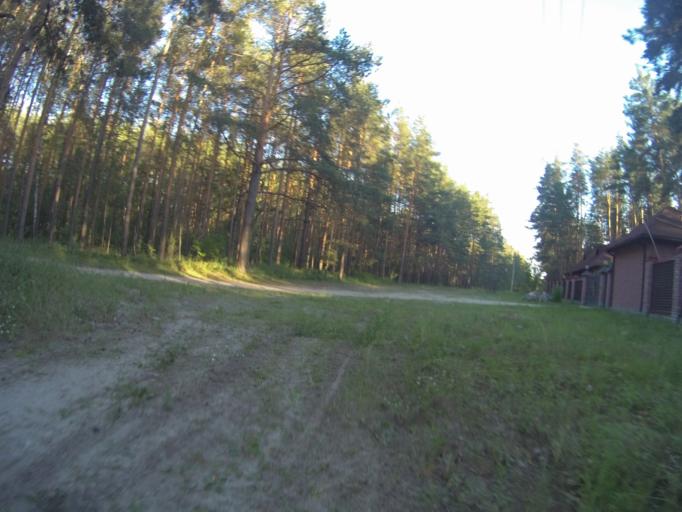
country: RU
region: Vladimir
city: Kommunar
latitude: 56.1422
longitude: 40.4932
